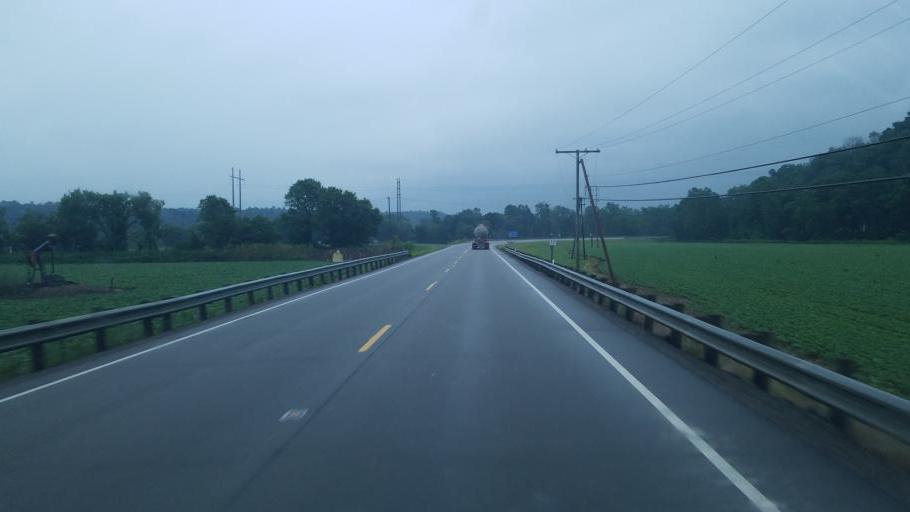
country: US
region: Ohio
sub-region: Coshocton County
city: Coshocton
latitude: 40.3026
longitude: -81.9016
